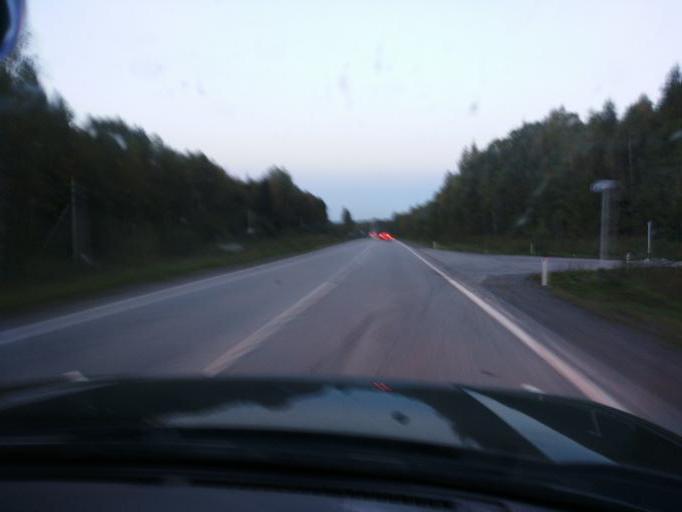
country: RU
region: Perm
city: Verkhnechusovskiye Gorodki
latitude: 58.2449
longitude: 57.0316
